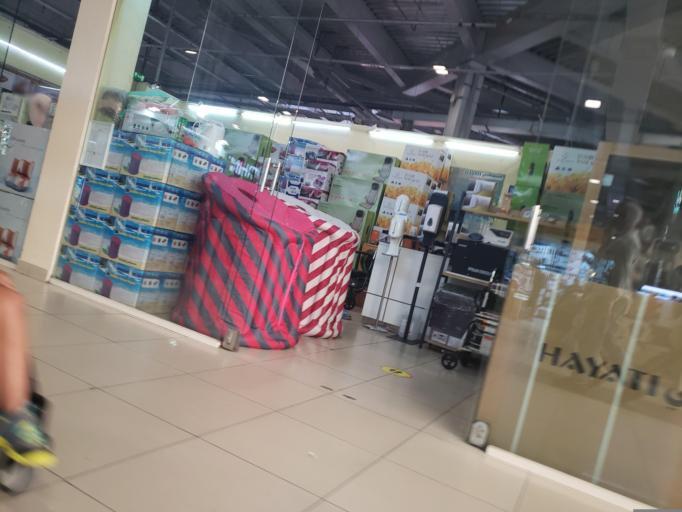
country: AE
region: Ash Shariqah
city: Sharjah
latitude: 25.1742
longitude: 55.4145
